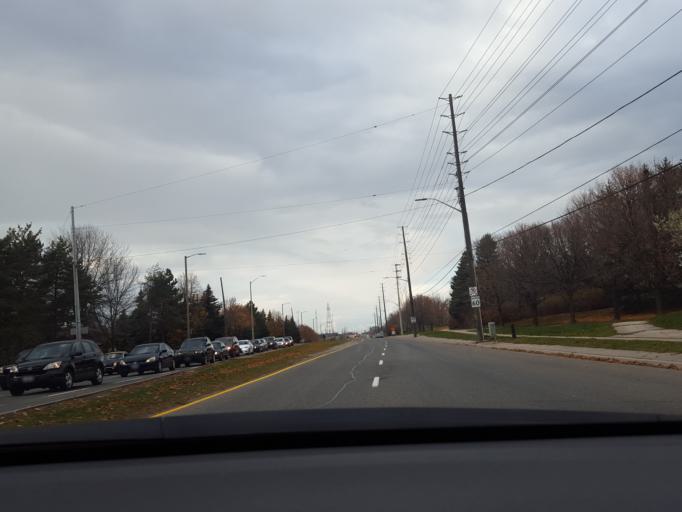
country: CA
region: Ontario
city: Mississauga
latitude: 43.5368
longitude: -79.7007
